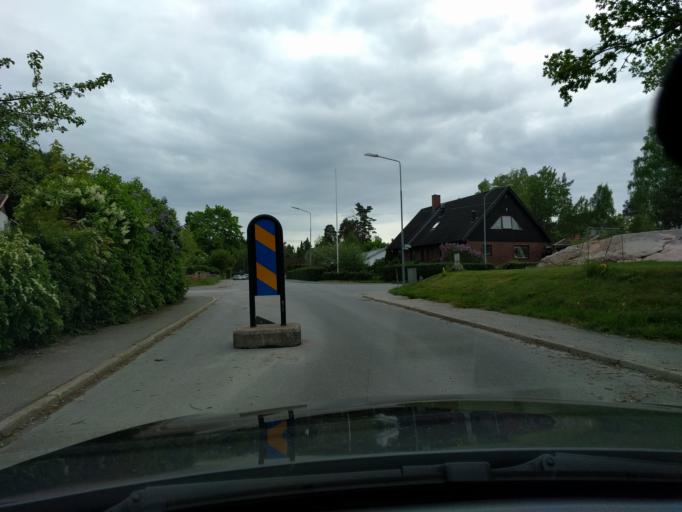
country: SE
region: Stockholm
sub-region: Taby Kommun
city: Taby
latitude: 59.4527
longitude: 18.0564
